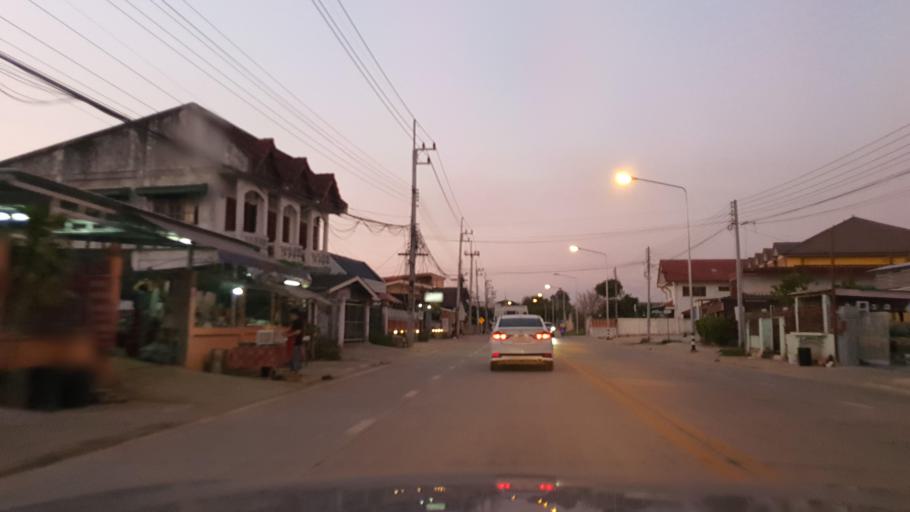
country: TH
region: Phayao
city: Dok Kham Tai
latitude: 19.1594
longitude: 99.9935
